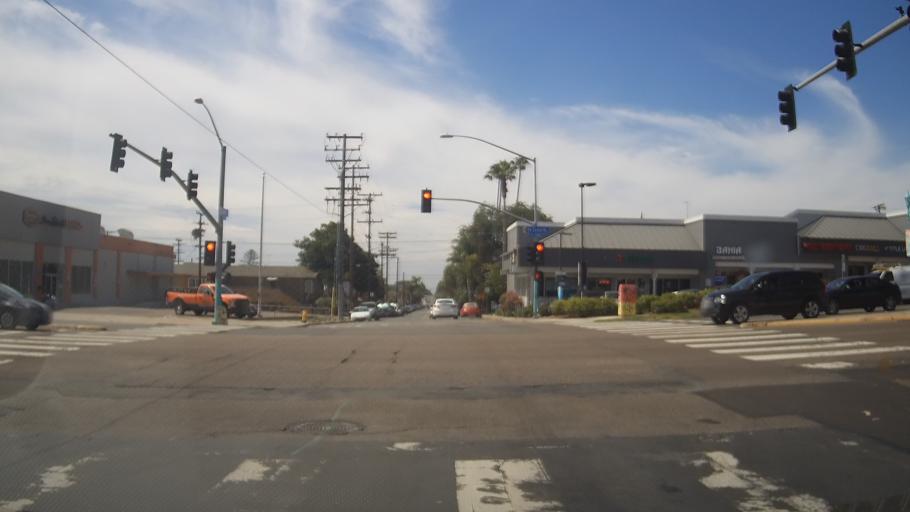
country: US
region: California
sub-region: San Diego County
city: San Diego
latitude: 32.7555
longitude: -117.1440
